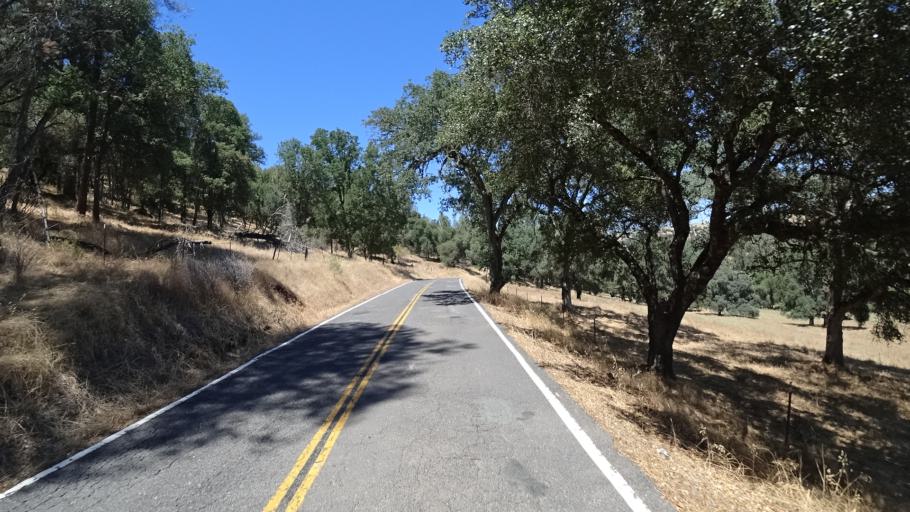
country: US
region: California
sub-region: Calaveras County
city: San Andreas
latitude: 38.1311
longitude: -120.6639
